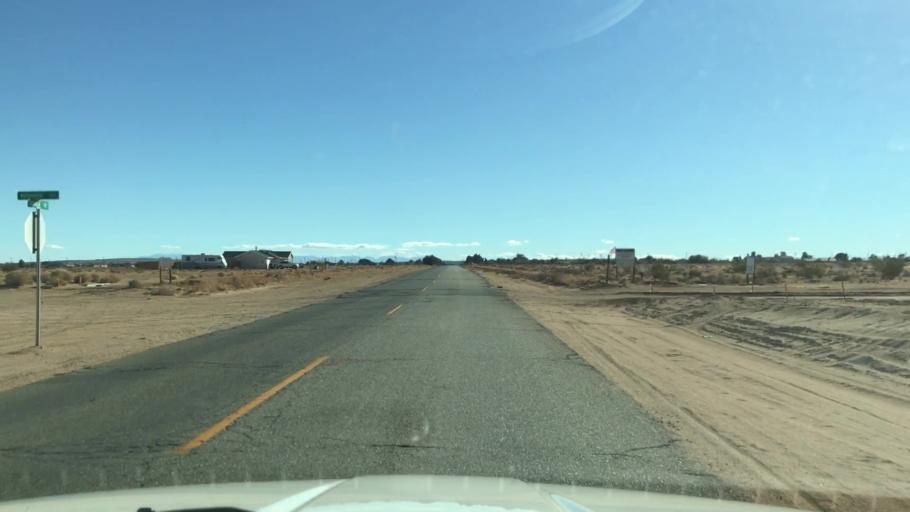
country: US
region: California
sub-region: Kern County
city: California City
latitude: 35.1406
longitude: -117.9859
